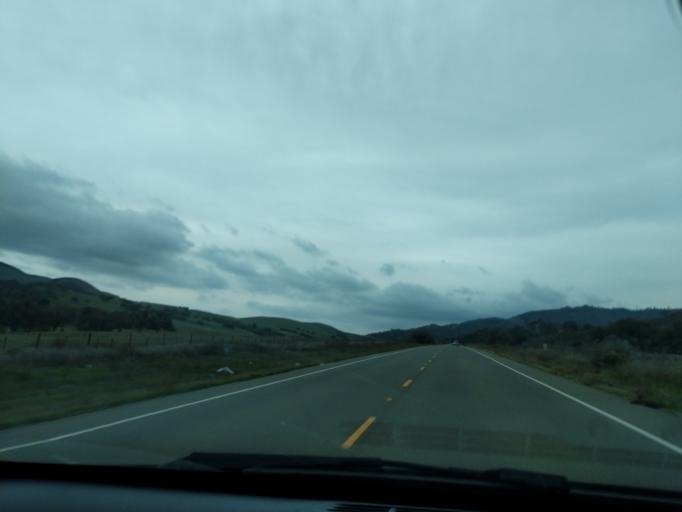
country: US
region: California
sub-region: Monterey County
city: Soledad
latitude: 36.6298
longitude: -121.2257
